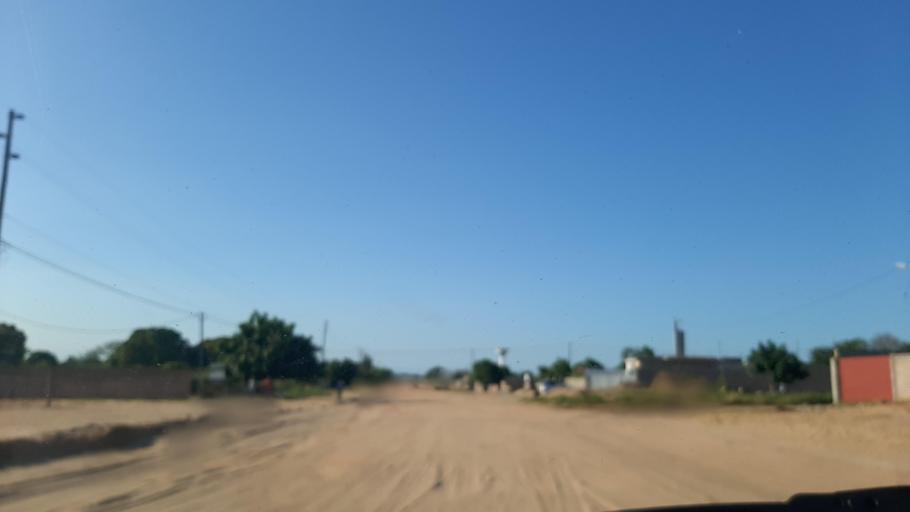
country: MZ
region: Maputo City
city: Maputo
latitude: -25.7949
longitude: 32.5522
